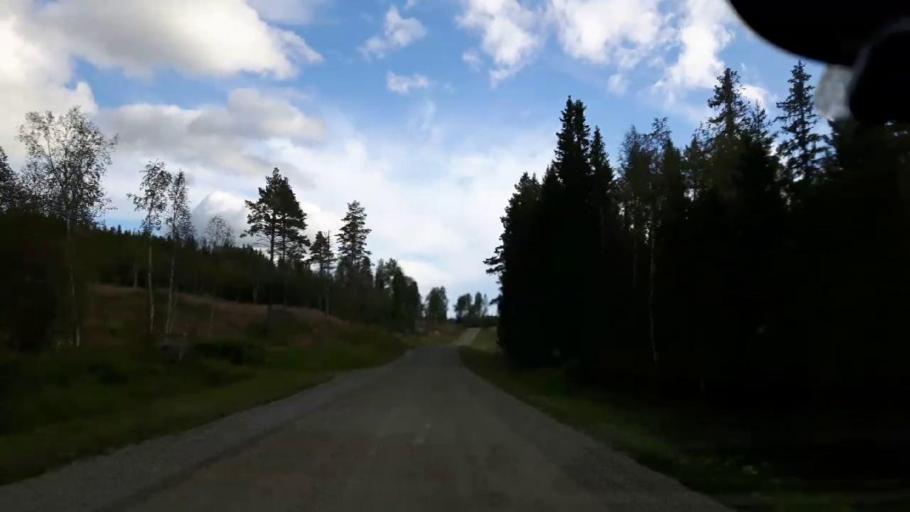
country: SE
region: Jaemtland
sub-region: Stroemsunds Kommun
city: Stroemsund
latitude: 63.3018
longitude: 15.6024
